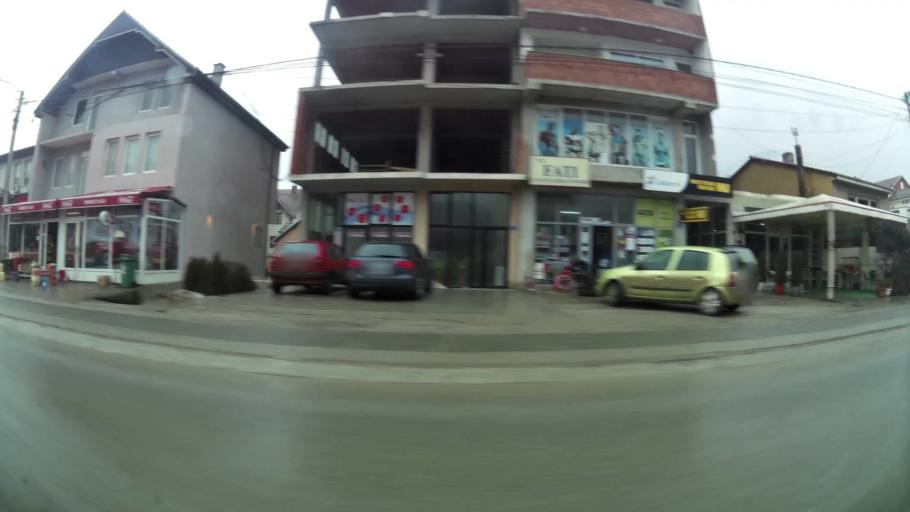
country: XK
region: Ferizaj
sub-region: Hani i Elezit
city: Hani i Elezit
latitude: 42.1515
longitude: 21.2976
